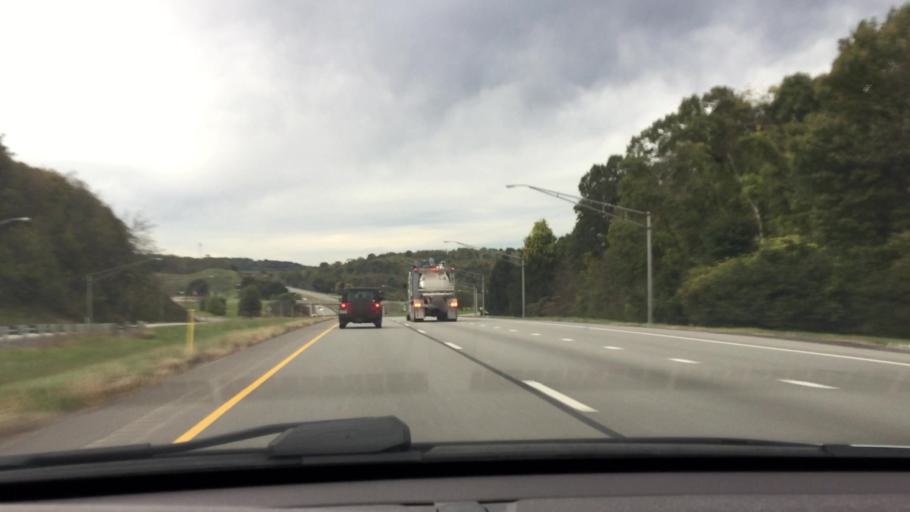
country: US
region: Pennsylvania
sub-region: Beaver County
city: Beaver
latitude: 40.6970
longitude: -80.3614
